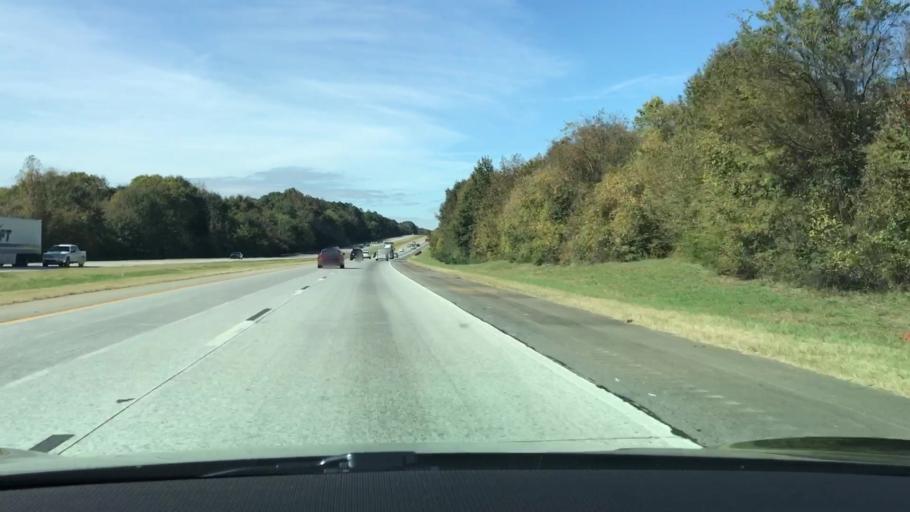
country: US
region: Georgia
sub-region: Morgan County
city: Madison
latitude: 33.5538
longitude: -83.4044
